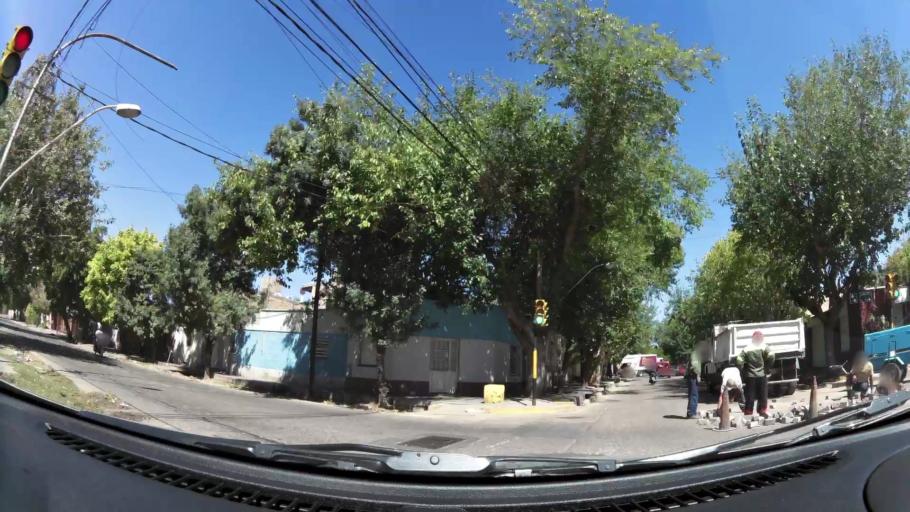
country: AR
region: Mendoza
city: Mendoza
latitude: -32.8851
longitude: -68.8182
